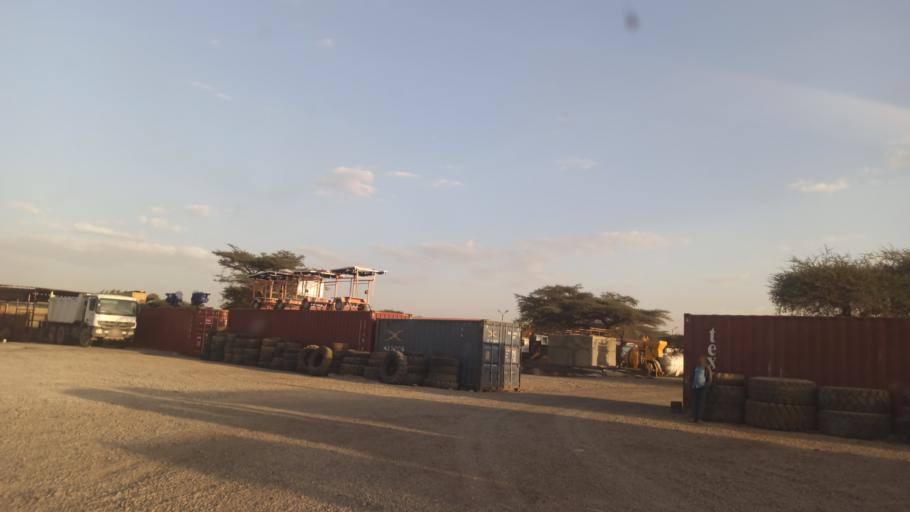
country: ET
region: Oromiya
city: Ziway
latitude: 7.7031
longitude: 38.6533
